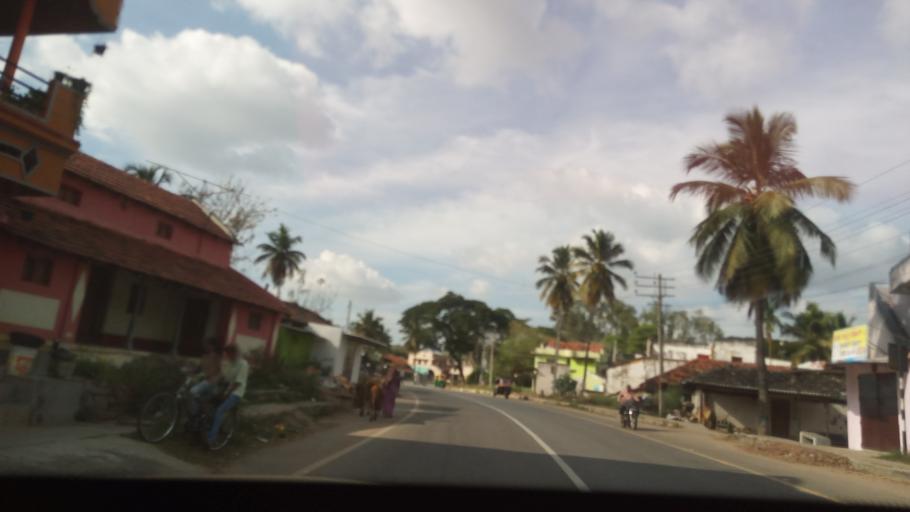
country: IN
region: Karnataka
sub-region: Mandya
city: Maddur
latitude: 12.6305
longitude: 77.0582
